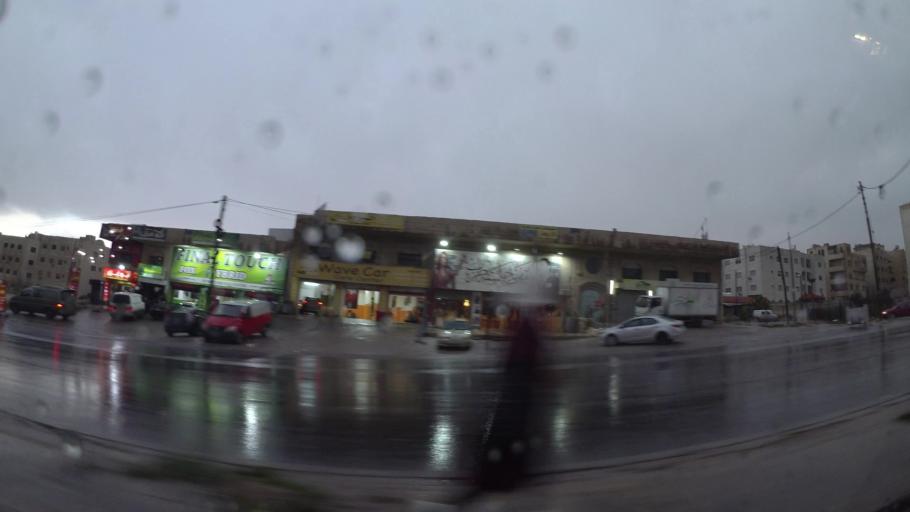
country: JO
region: Amman
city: Amman
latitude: 31.9887
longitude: 35.9602
